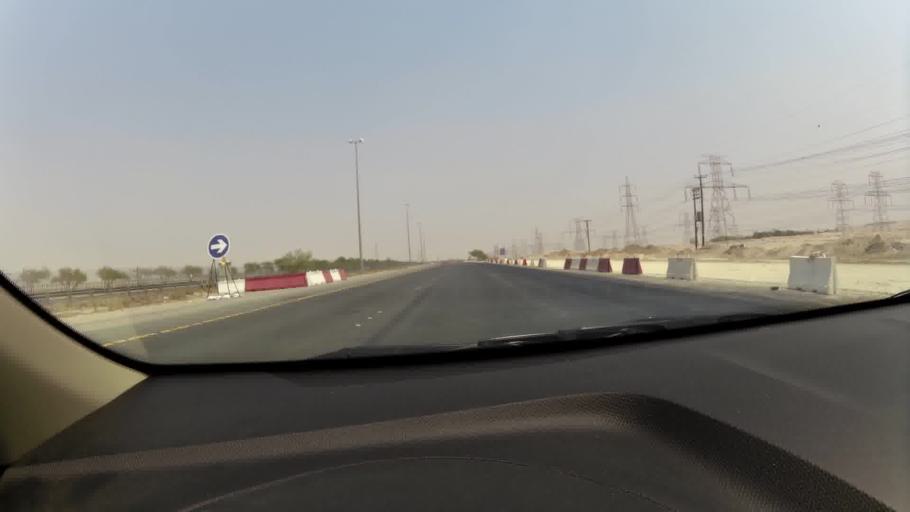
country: KW
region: Al Farwaniyah
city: Al Farwaniyah
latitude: 29.1824
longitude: 47.9123
